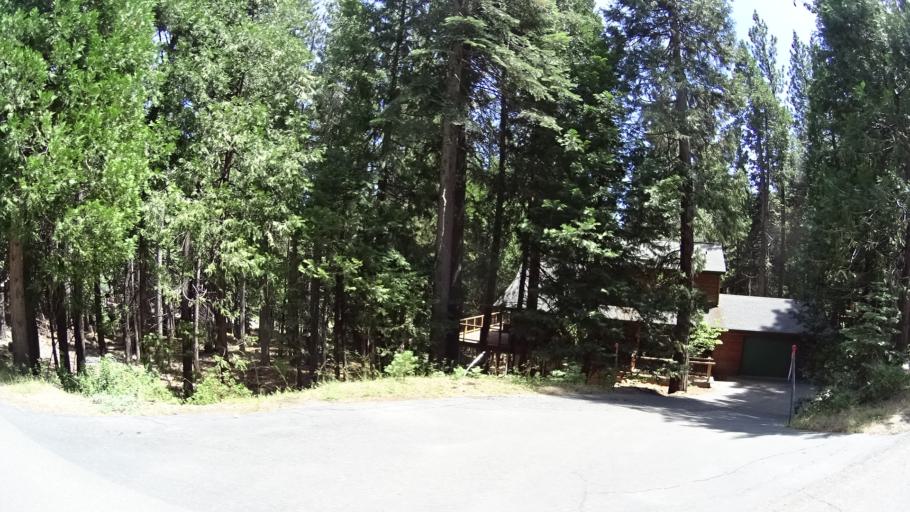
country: US
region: California
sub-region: Calaveras County
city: Arnold
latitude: 38.3066
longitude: -120.2630
